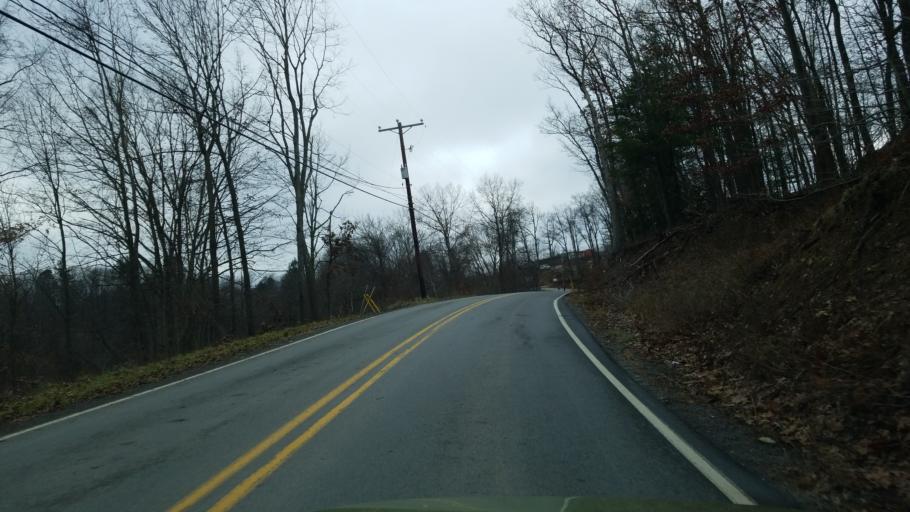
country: US
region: Pennsylvania
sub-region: Clearfield County
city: Clearfield
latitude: 41.0334
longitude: -78.4647
